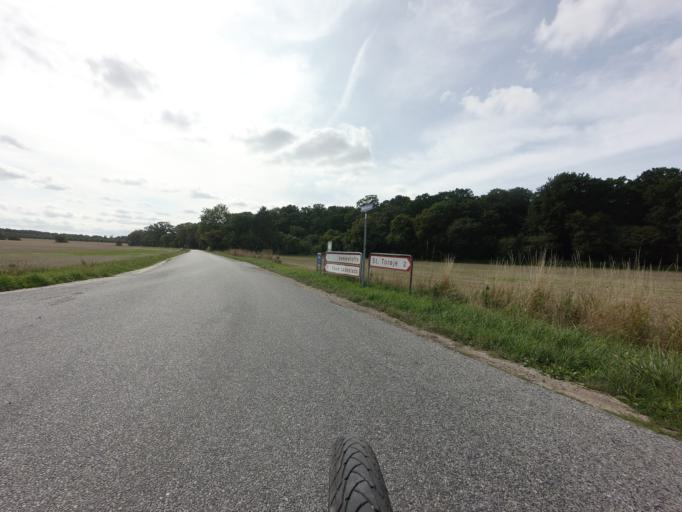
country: DK
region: Zealand
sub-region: Faxe Kommune
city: Fakse Ladeplads
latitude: 55.2530
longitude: 12.2356
